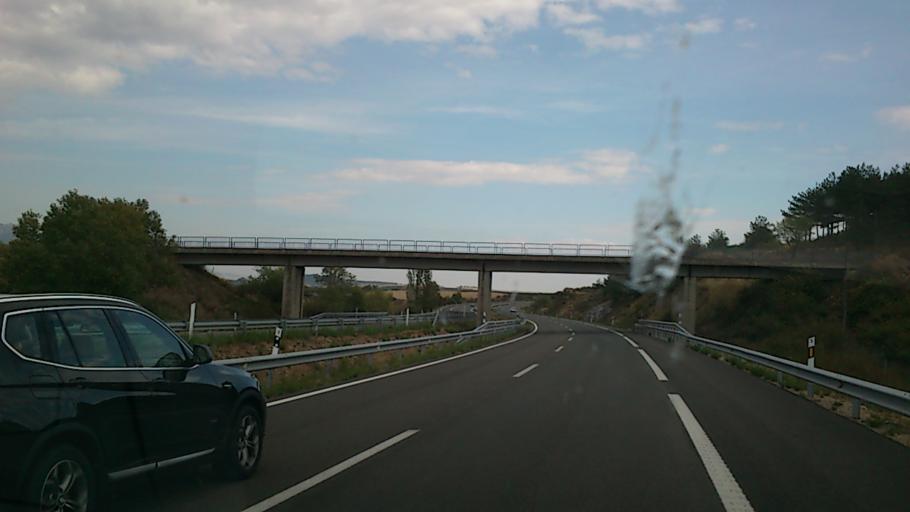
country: ES
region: La Rioja
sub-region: Provincia de La Rioja
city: Briones
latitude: 42.5233
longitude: -2.7772
